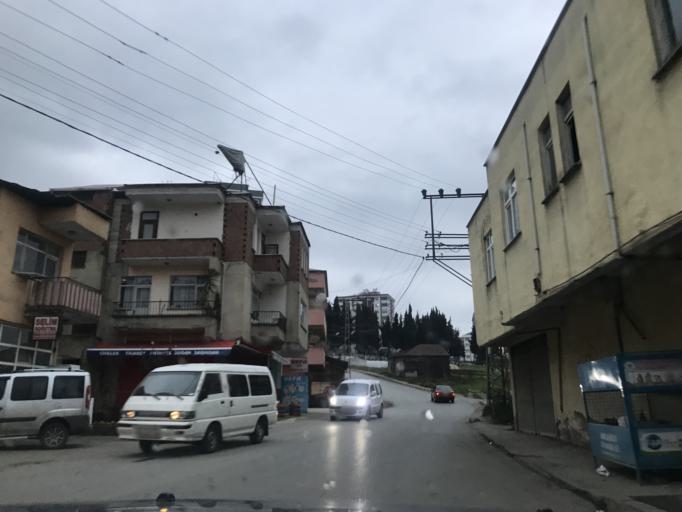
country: TR
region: Trabzon
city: Akcaabat
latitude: 41.0110
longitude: 39.5908
